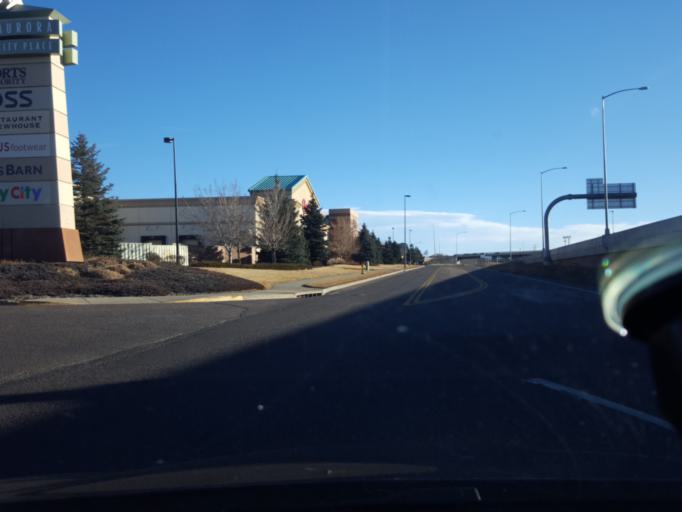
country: US
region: Colorado
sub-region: Adams County
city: Aurora
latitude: 39.7161
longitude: -104.8264
